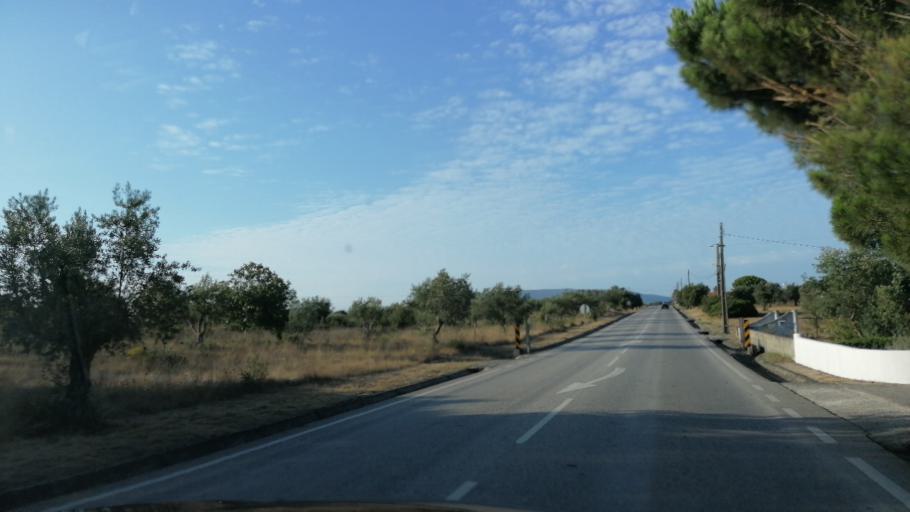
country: PT
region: Santarem
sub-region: Alcanena
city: Alcanena
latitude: 39.4159
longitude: -8.6369
